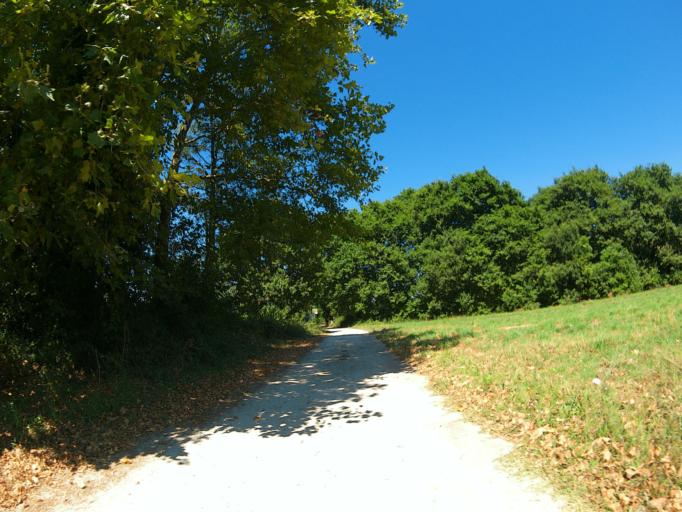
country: PT
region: Viana do Castelo
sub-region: Viana do Castelo
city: Darque
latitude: 41.7132
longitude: -8.7069
